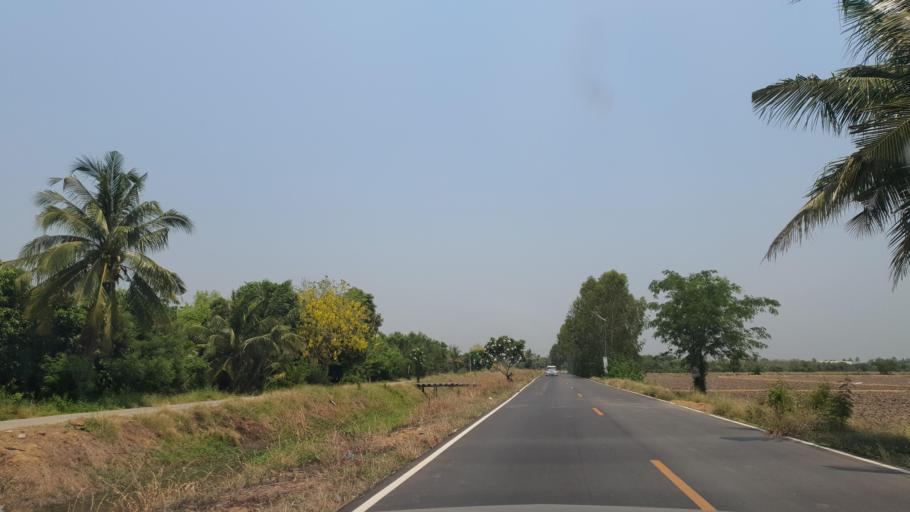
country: TH
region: Suphan Buri
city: Si Prachan
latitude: 14.6124
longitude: 100.1011
